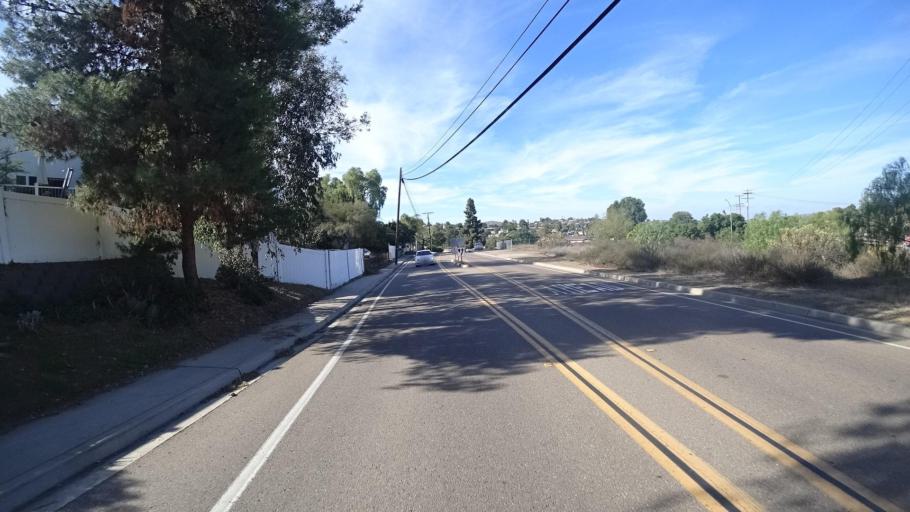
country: US
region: California
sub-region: San Diego County
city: Casa de Oro-Mount Helix
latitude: 32.7439
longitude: -116.9641
